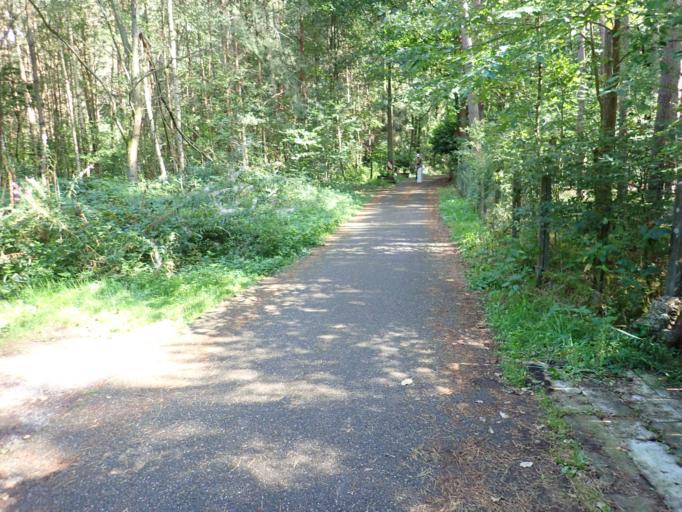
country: BE
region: Flanders
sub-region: Provincie Antwerpen
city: Olen
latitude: 51.1356
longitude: 4.8925
